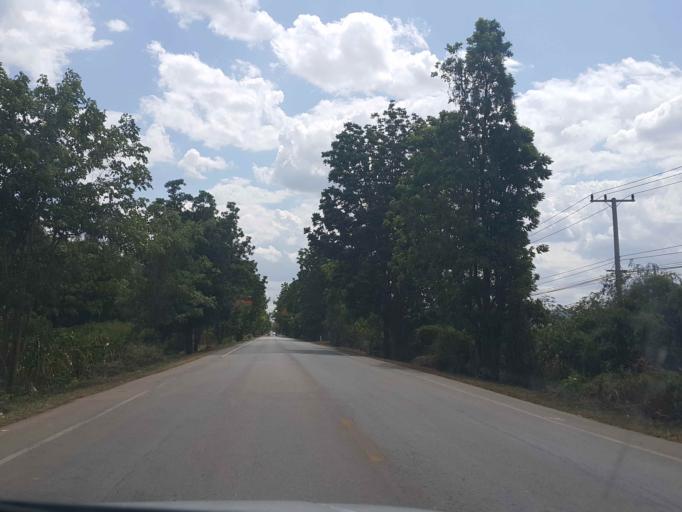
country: TH
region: Sukhothai
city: Thung Saliam
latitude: 17.3367
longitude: 99.5786
